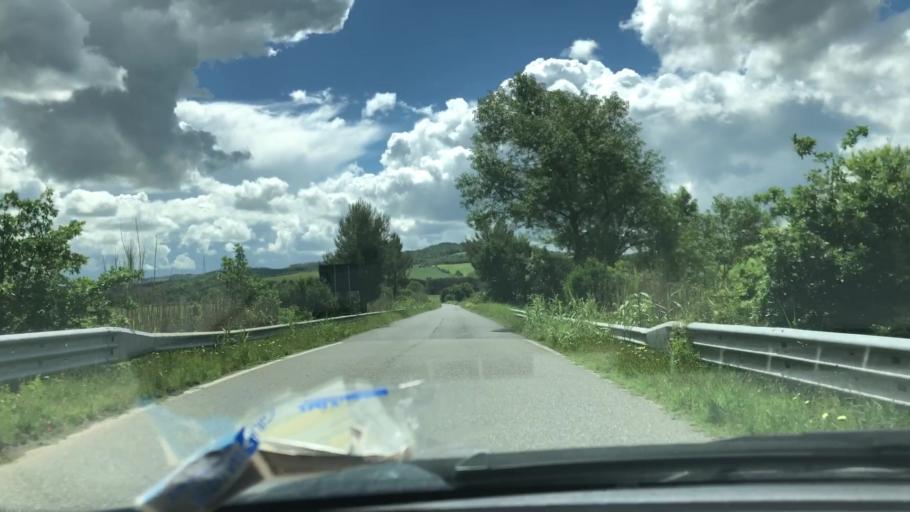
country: IT
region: Tuscany
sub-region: Province of Pisa
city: Saline
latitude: 43.3536
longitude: 10.7863
